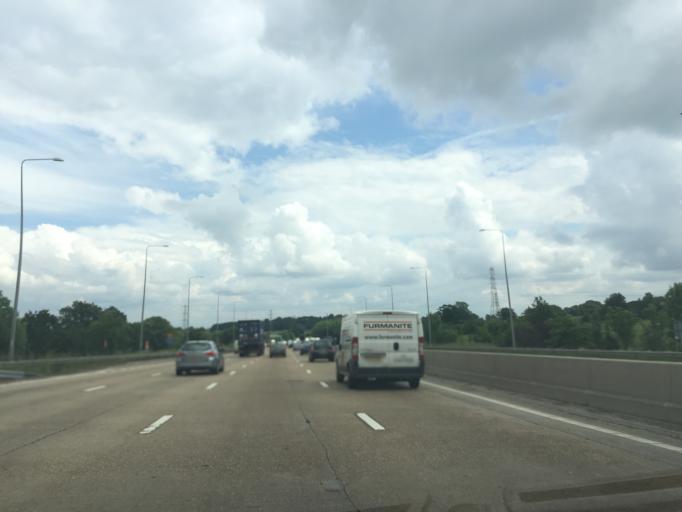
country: GB
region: England
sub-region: Hertfordshire
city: Potters Bar
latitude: 51.6873
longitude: -0.1595
